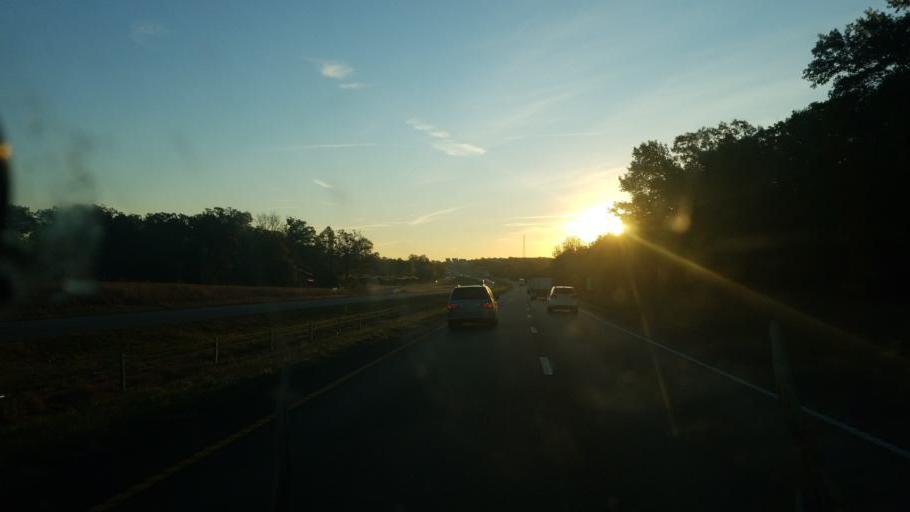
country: US
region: Missouri
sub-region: Boone County
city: Hallsville
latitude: 38.9556
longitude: -92.1601
